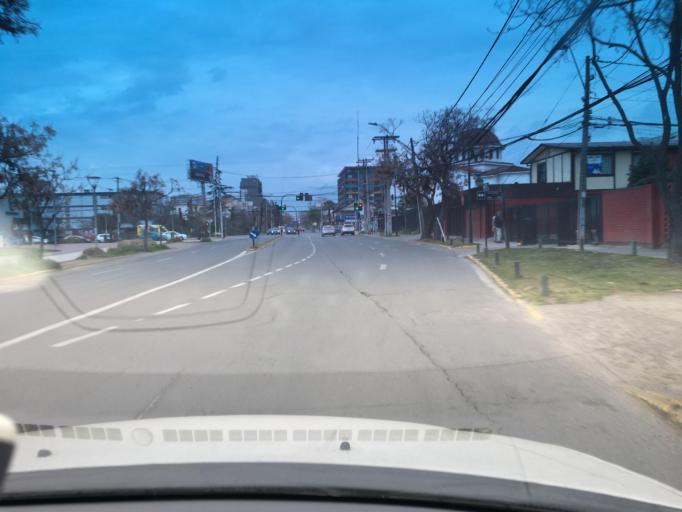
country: CL
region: Santiago Metropolitan
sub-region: Provincia de Santiago
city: Villa Presidente Frei, Nunoa, Santiago, Chile
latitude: -33.4633
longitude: -70.6063
